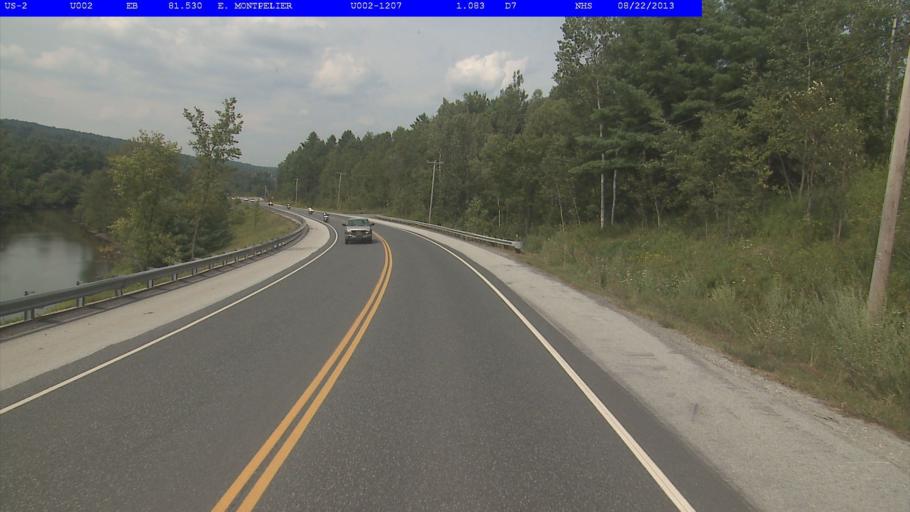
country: US
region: Vermont
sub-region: Washington County
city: Barre
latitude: 44.2488
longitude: -72.5009
